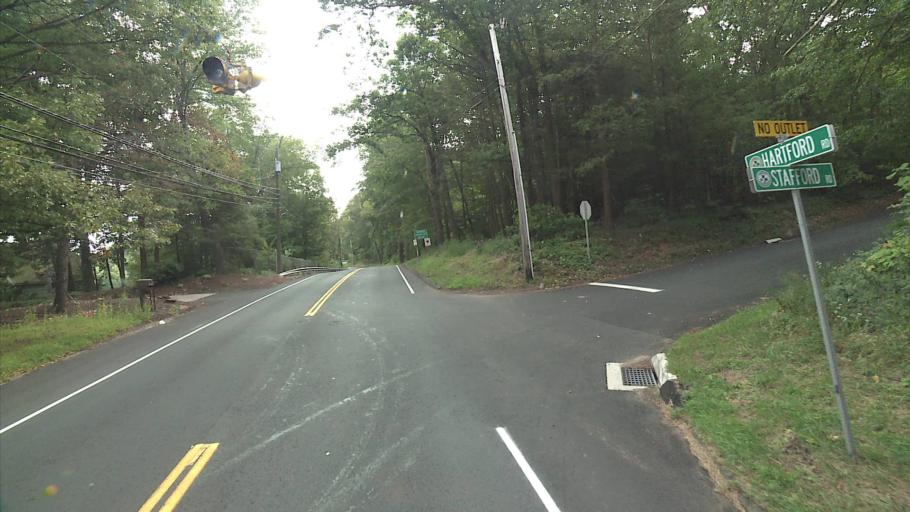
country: US
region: Connecticut
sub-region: Hartford County
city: Weatogue
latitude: 41.8379
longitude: -72.7850
